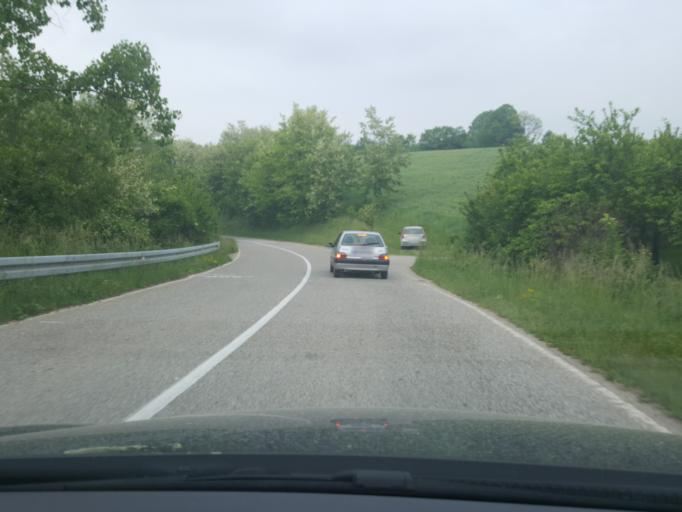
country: RS
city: Kamenica
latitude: 44.2469
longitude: 19.7430
